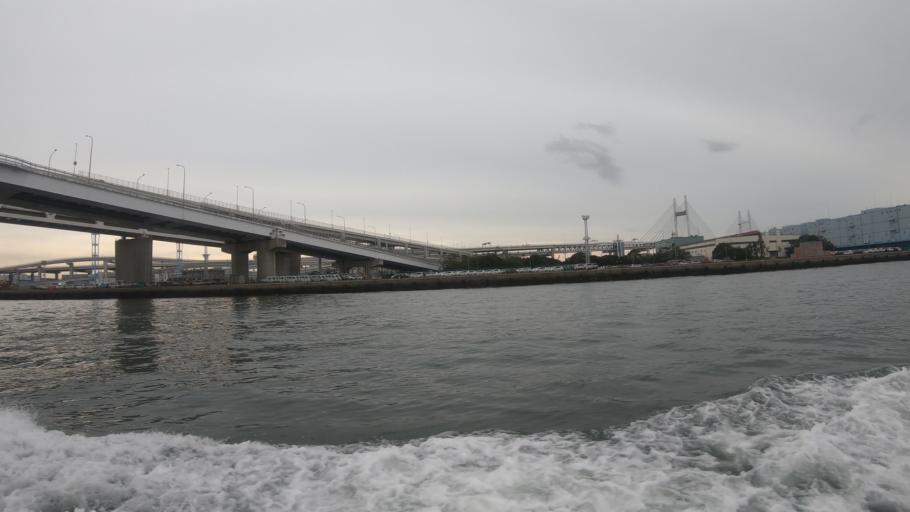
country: JP
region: Kanagawa
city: Yokohama
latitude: 35.4673
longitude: 139.6753
